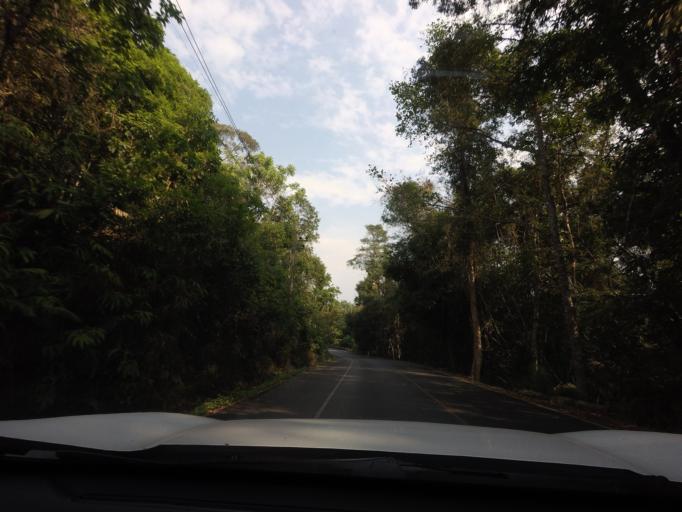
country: TH
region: Nakhon Ratchasima
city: Pak Chong
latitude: 14.4255
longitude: 101.3924
